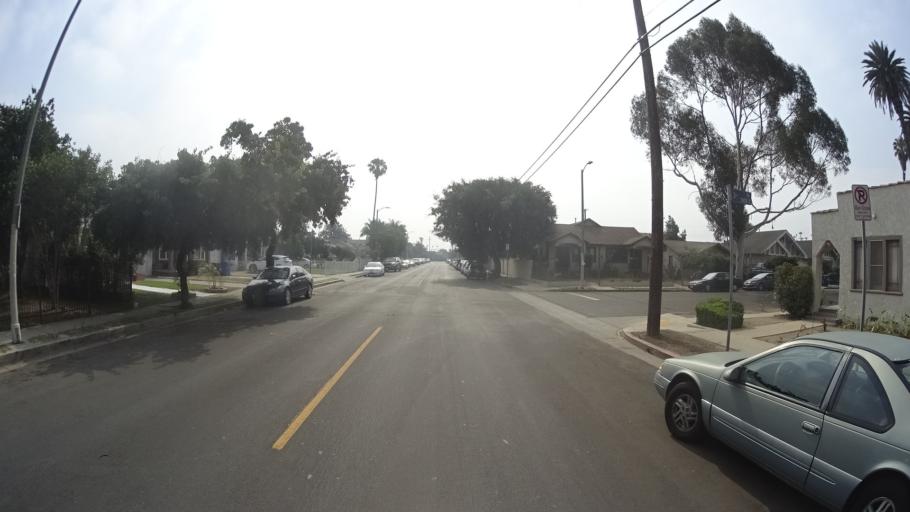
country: US
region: California
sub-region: Los Angeles County
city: View Park-Windsor Hills
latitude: 34.0296
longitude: -118.3205
